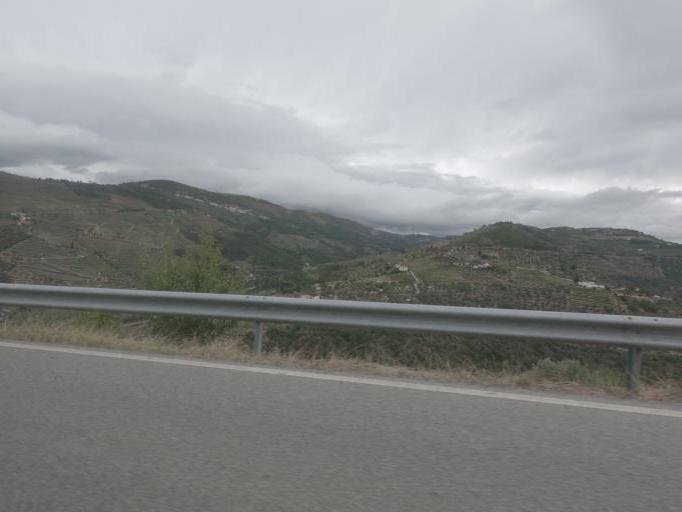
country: PT
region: Vila Real
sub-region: Sabrosa
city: Vilela
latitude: 41.1988
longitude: -7.5403
